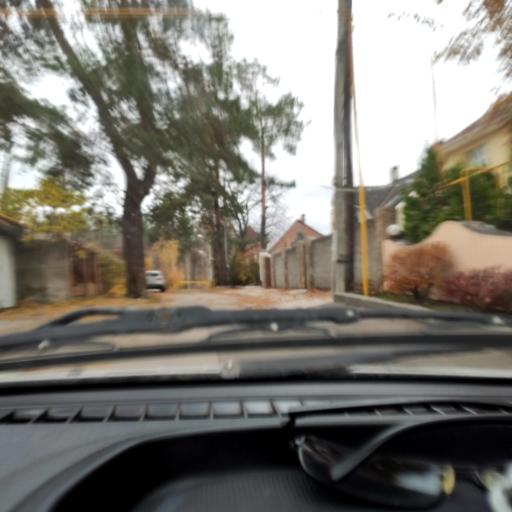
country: RU
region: Samara
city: Tol'yatti
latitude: 53.4804
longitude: 49.3554
